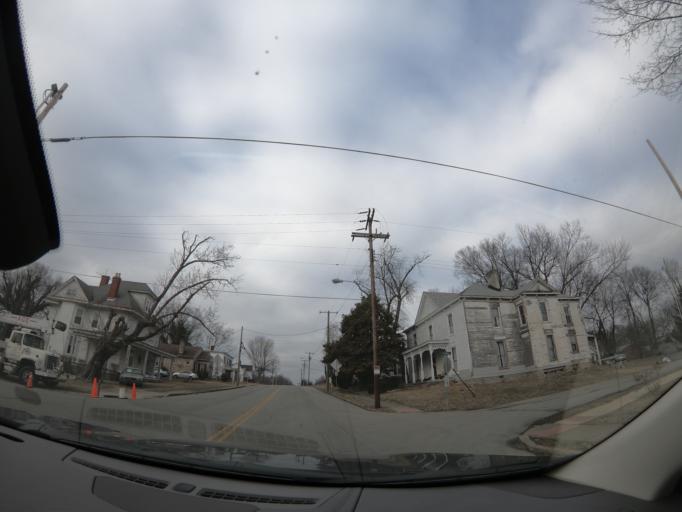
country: US
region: Kentucky
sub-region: Spencer County
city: Taylorsville
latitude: 37.9134
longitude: -85.3177
